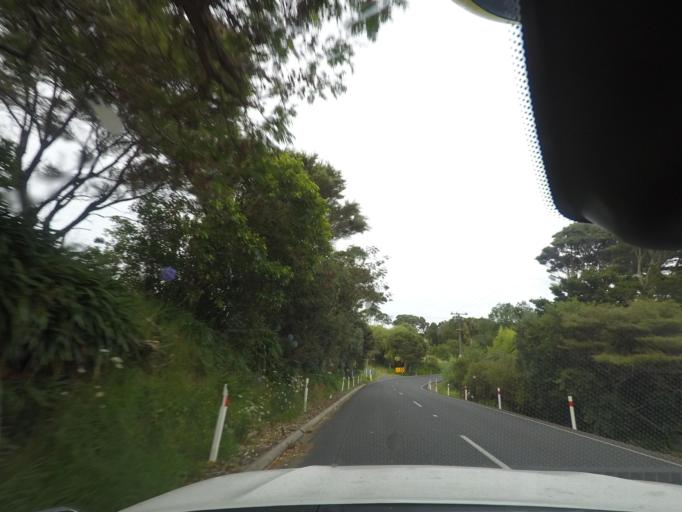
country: NZ
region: Auckland
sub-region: Auckland
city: Parakai
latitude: -36.5191
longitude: 174.2614
